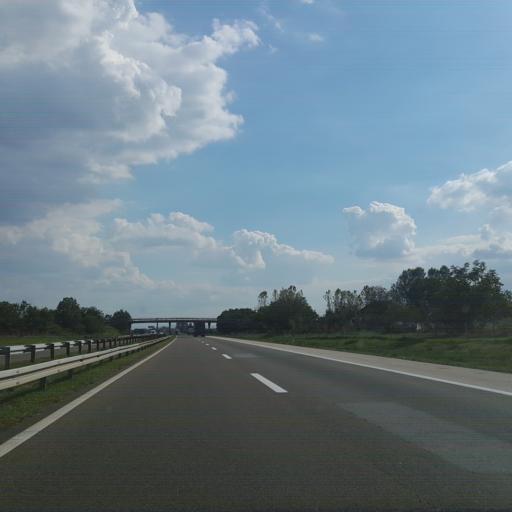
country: RS
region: Central Serbia
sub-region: Podunavski Okrug
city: Velika Plana
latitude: 44.3105
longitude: 21.0934
